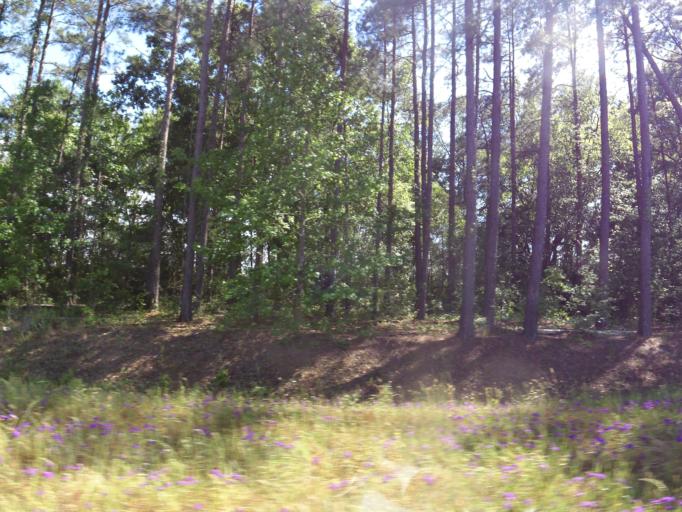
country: US
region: South Carolina
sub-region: Bamberg County
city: Denmark
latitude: 33.3431
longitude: -81.1889
